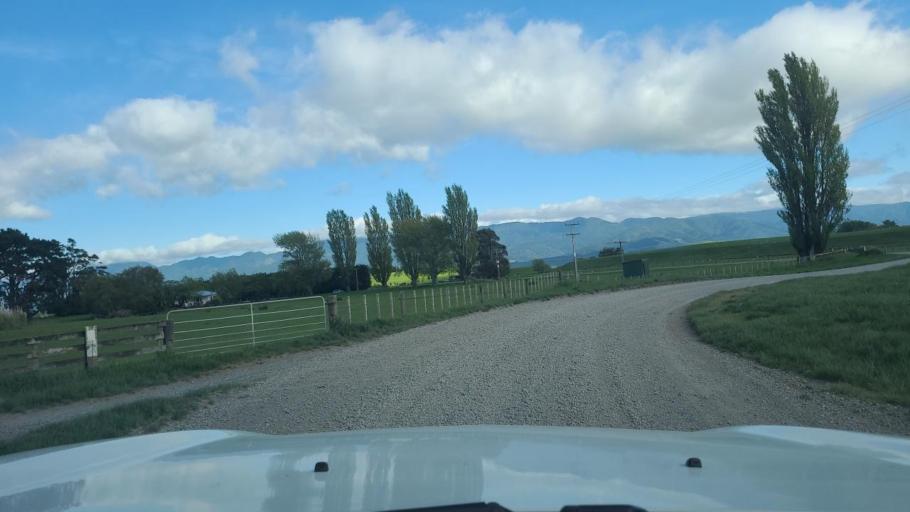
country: NZ
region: Wellington
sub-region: Upper Hutt City
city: Upper Hutt
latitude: -41.3438
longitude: 175.2044
